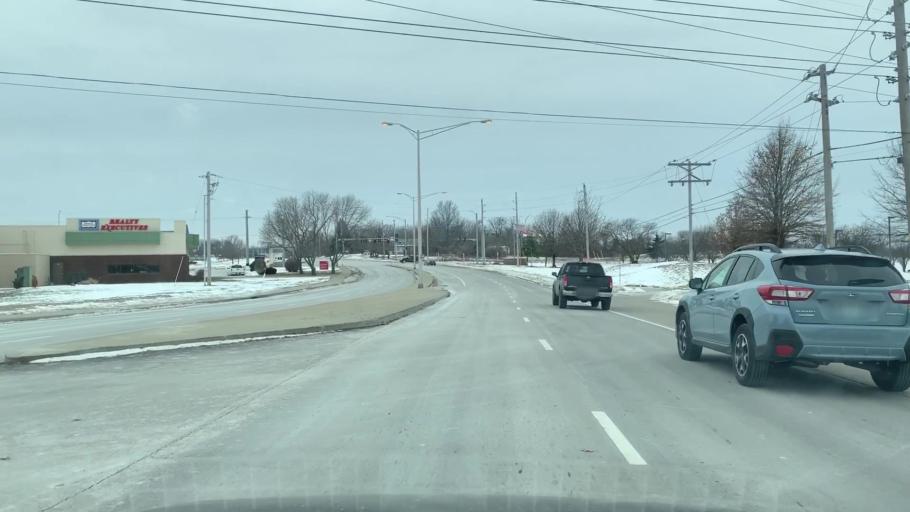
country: US
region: Missouri
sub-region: Jackson County
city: Lees Summit
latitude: 38.9323
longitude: -94.3790
